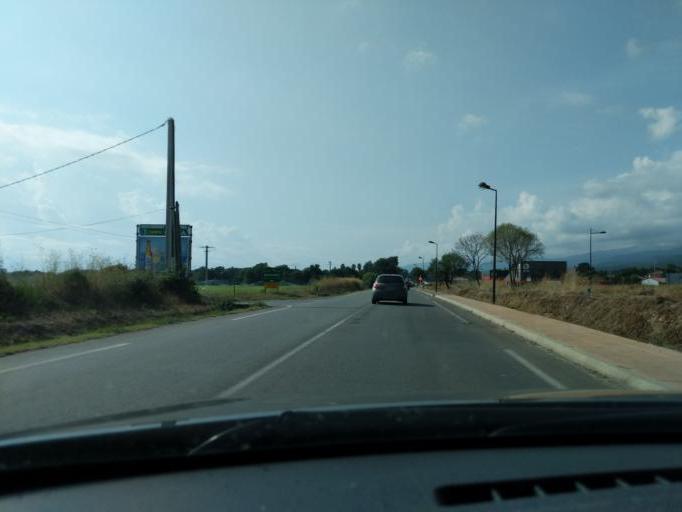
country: FR
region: Corsica
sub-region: Departement de la Haute-Corse
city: Ghisonaccia
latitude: 41.9921
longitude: 9.4021
